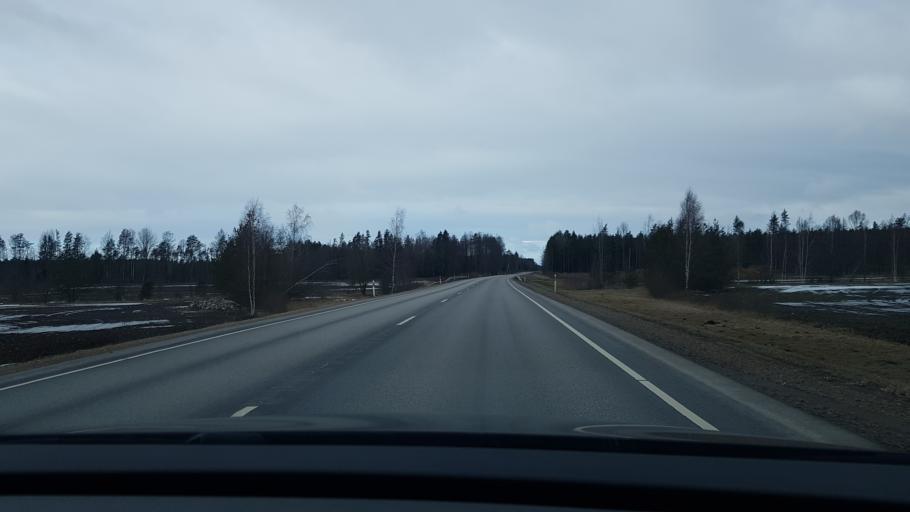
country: EE
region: Paernumaa
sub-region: Paikuse vald
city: Paikuse
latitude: 58.2755
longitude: 24.6248
